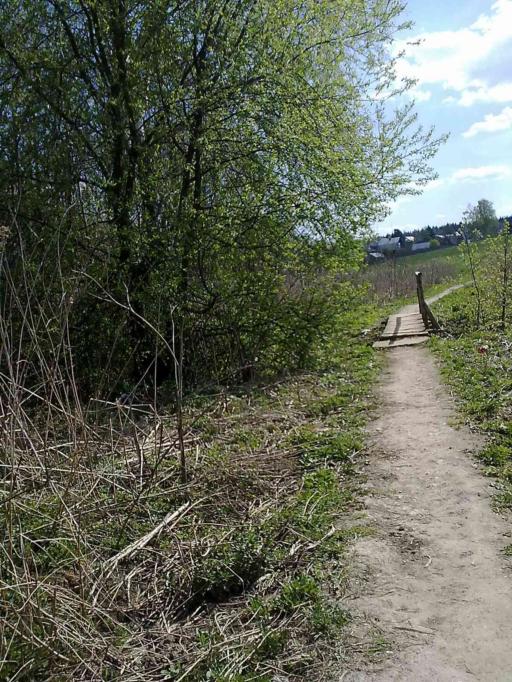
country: RU
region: Moskovskaya
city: Lesnoy Gorodok
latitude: 55.6516
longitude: 37.1906
